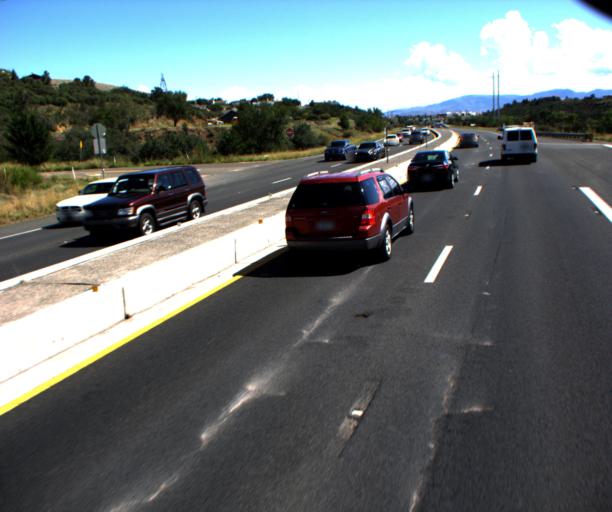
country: US
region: Arizona
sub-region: Yavapai County
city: Prescott Valley
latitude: 34.5617
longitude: -112.3772
